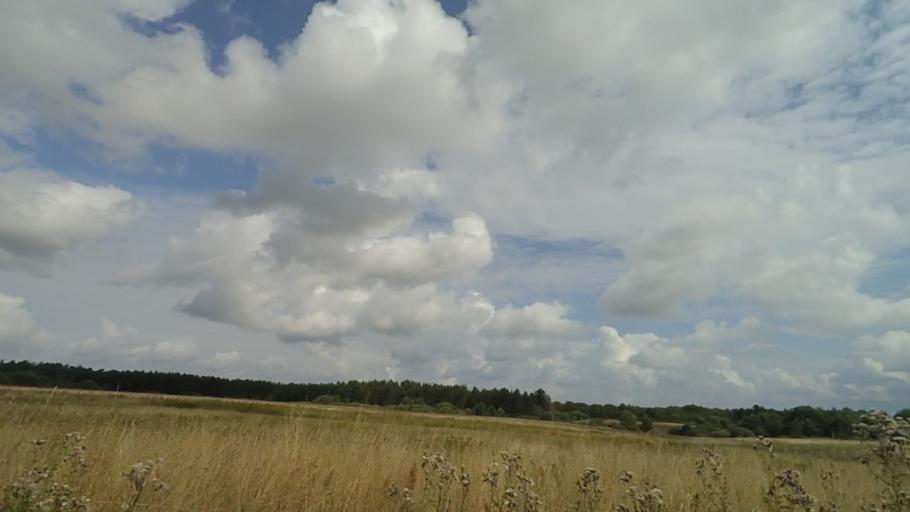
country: DK
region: Central Jutland
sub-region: Syddjurs Kommune
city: Ryomgard
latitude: 56.4774
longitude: 10.4979
